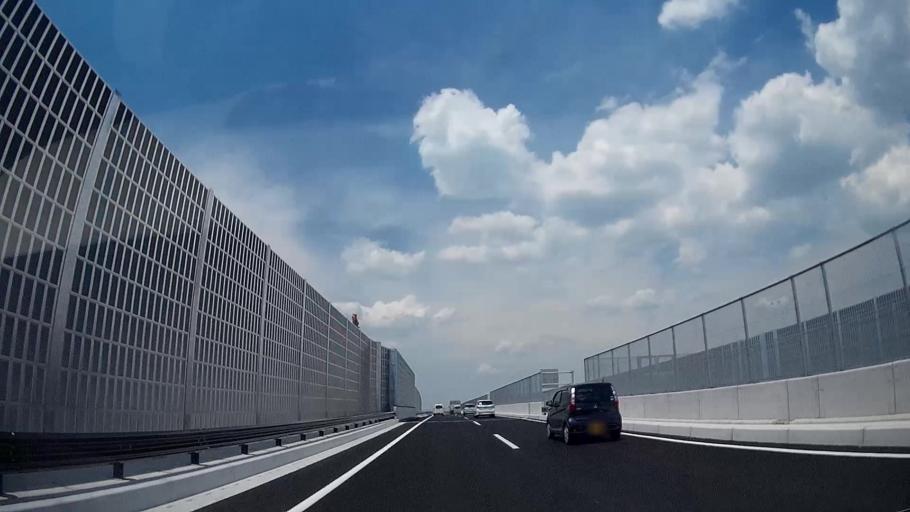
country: JP
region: Chiba
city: Matsudo
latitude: 35.7345
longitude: 139.9201
